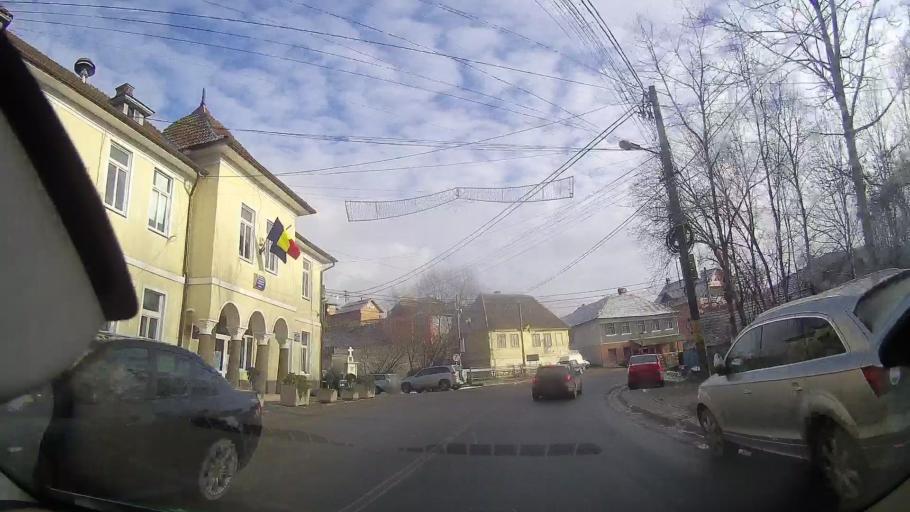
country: RO
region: Alba
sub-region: Comuna Bistra
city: Bistra
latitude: 46.3788
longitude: 23.0989
